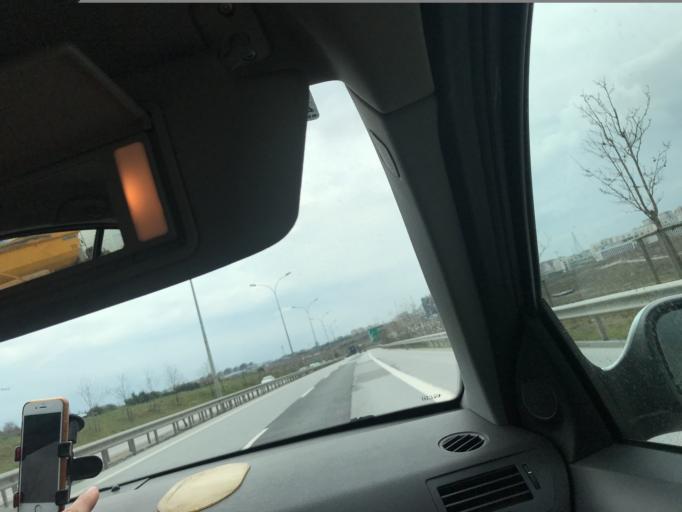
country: TR
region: Istanbul
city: Sultanbeyli
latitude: 40.9244
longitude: 29.3248
